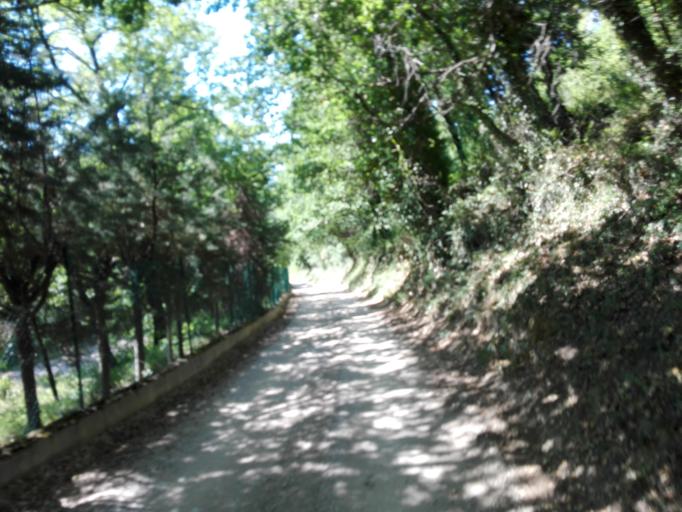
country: IT
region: Umbria
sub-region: Provincia di Perugia
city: Foligno
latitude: 42.9700
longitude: 12.7422
